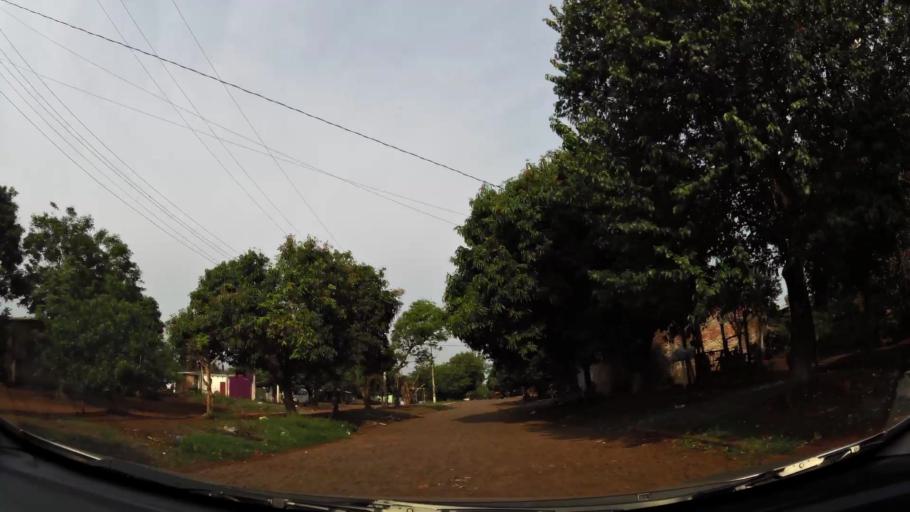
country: PY
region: Alto Parana
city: Ciudad del Este
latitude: -25.4813
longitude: -54.6693
